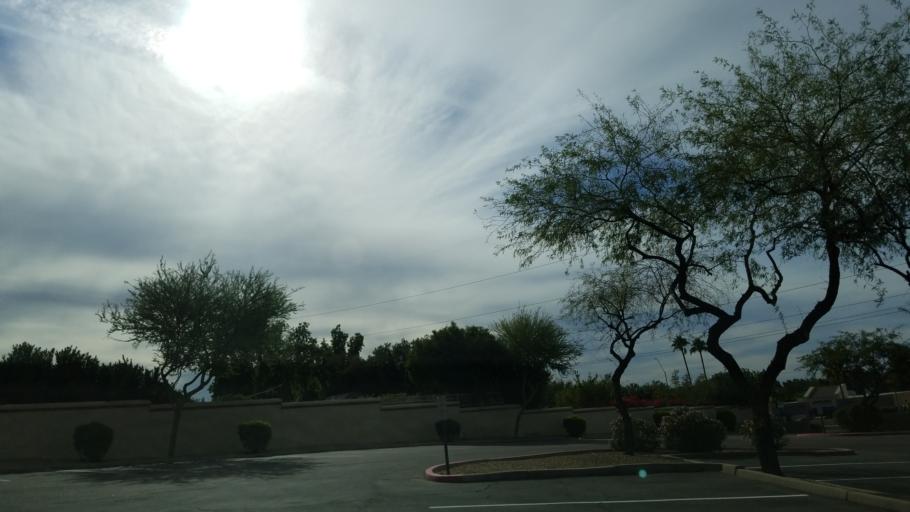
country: US
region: Arizona
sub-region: Maricopa County
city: Glendale
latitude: 33.6289
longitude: -112.0642
